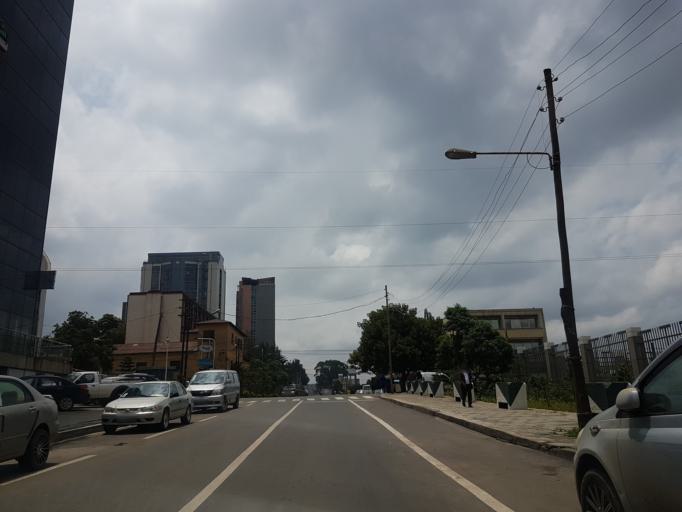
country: ET
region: Adis Abeba
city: Addis Ababa
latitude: 9.0026
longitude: 38.7449
